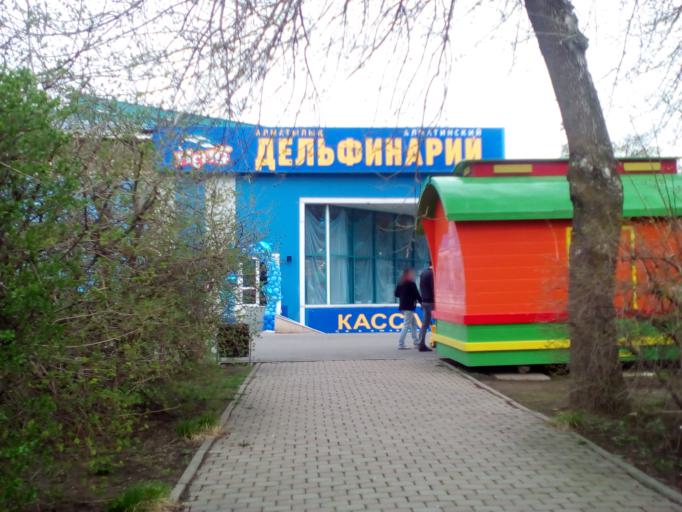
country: KZ
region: Almaty Qalasy
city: Almaty
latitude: 43.2626
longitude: 76.9706
